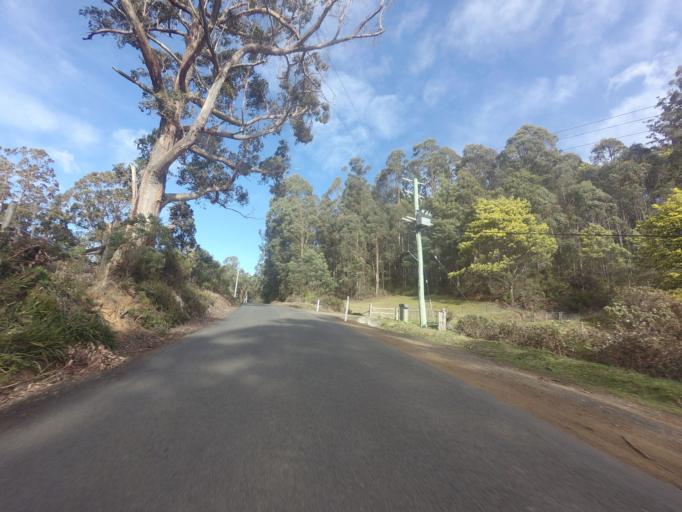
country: AU
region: Tasmania
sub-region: Kingborough
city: Margate
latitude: -43.0096
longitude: 147.1667
